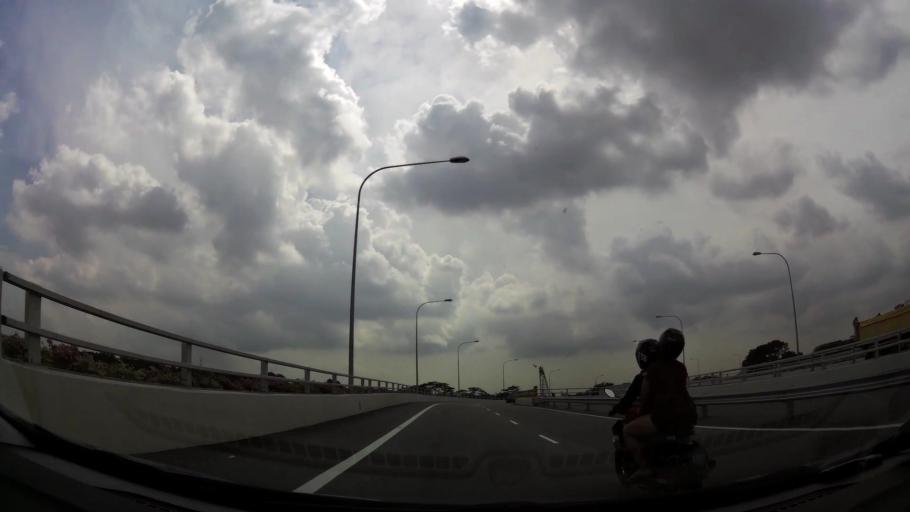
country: MY
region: Johor
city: Kampung Pasir Gudang Baru
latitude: 1.3999
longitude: 103.8570
